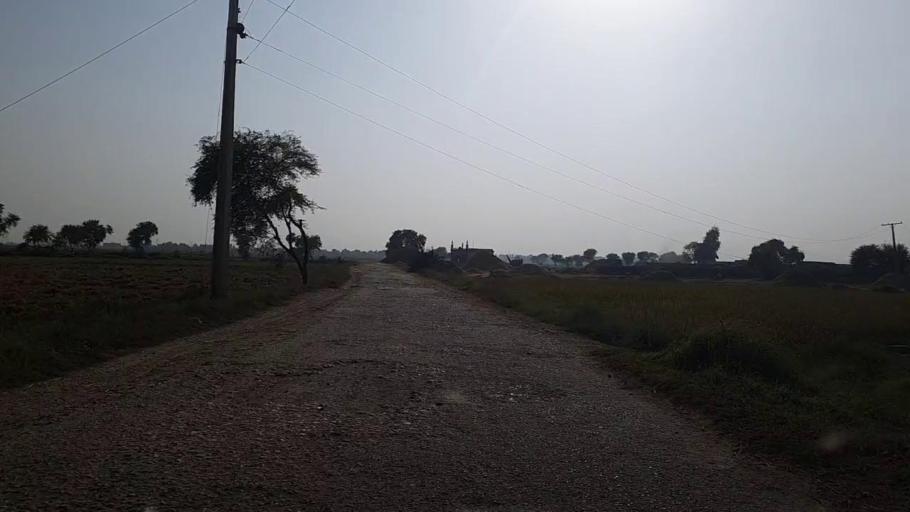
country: PK
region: Sindh
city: Kandhkot
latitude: 28.2851
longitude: 69.2578
